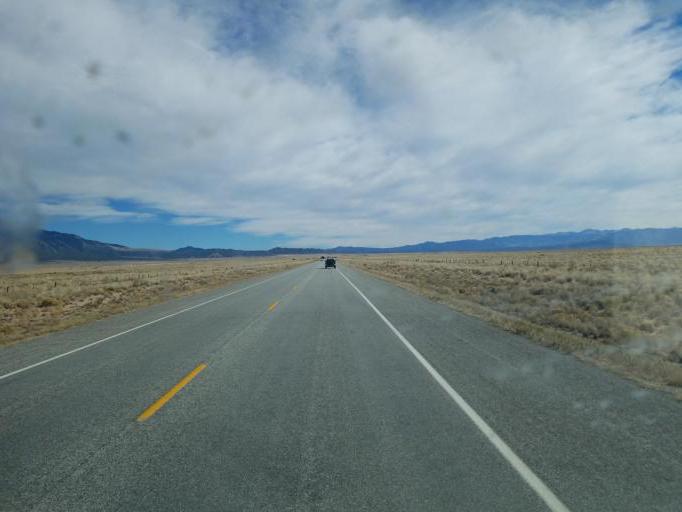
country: US
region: Colorado
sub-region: Alamosa County
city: Alamosa East
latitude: 37.4750
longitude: -105.6289
